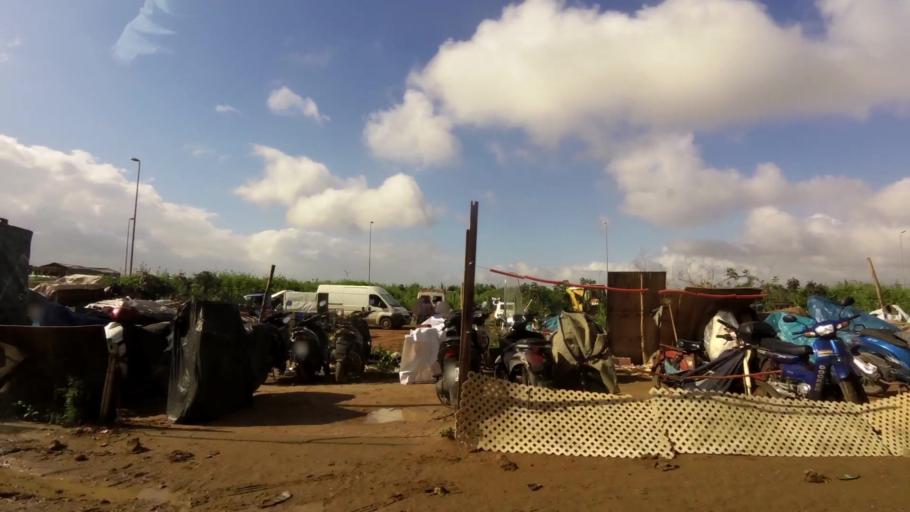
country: MA
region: Grand Casablanca
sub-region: Nouaceur
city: Bouskoura
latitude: 33.5329
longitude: -7.7026
